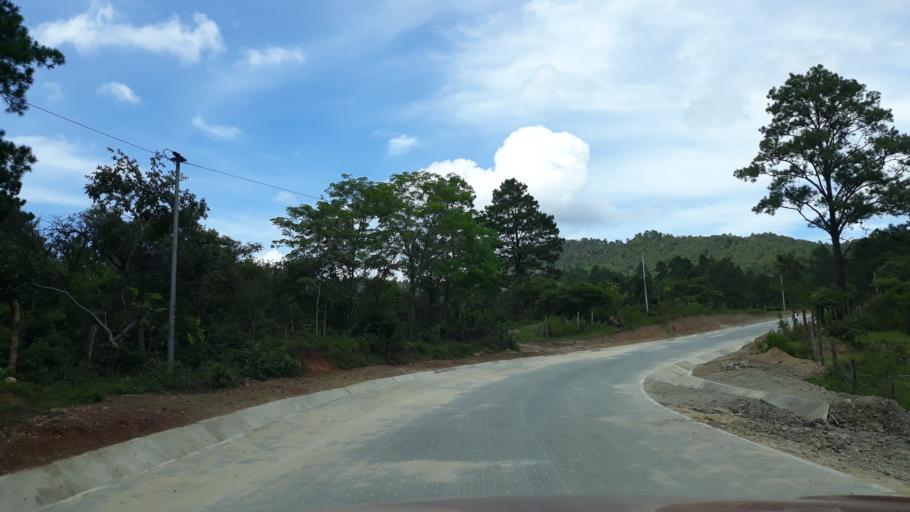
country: HN
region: El Paraiso
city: Santa Cruz
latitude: 13.7459
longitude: -86.6272
